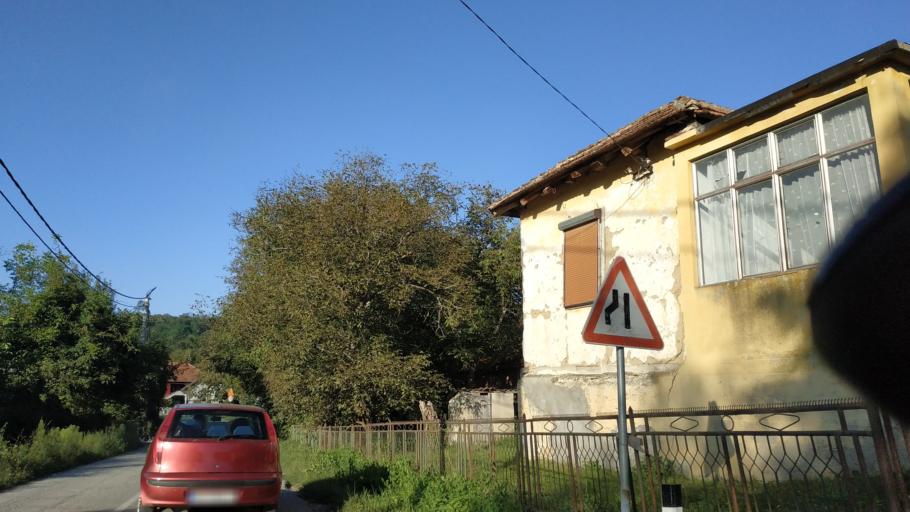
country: RS
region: Central Serbia
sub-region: Rasinski Okrug
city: Krusevac
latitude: 43.4966
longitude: 21.3414
